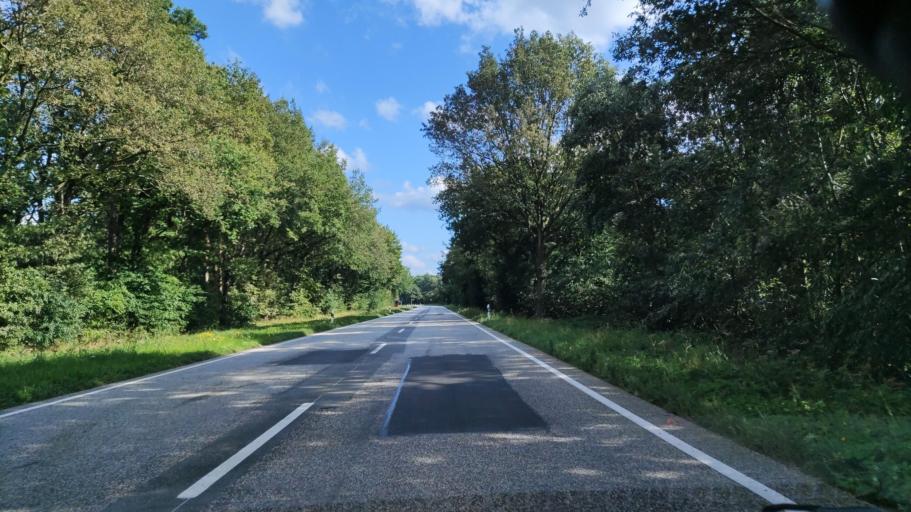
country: DE
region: Schleswig-Holstein
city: Brammer
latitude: 54.2179
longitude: 9.7201
